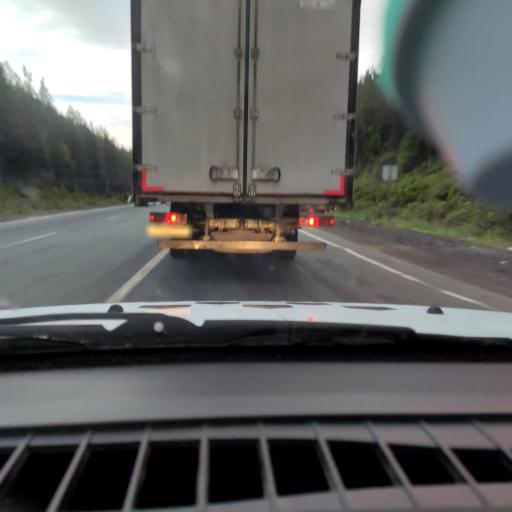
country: RU
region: Sverdlovsk
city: Revda
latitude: 56.8341
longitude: 59.8381
